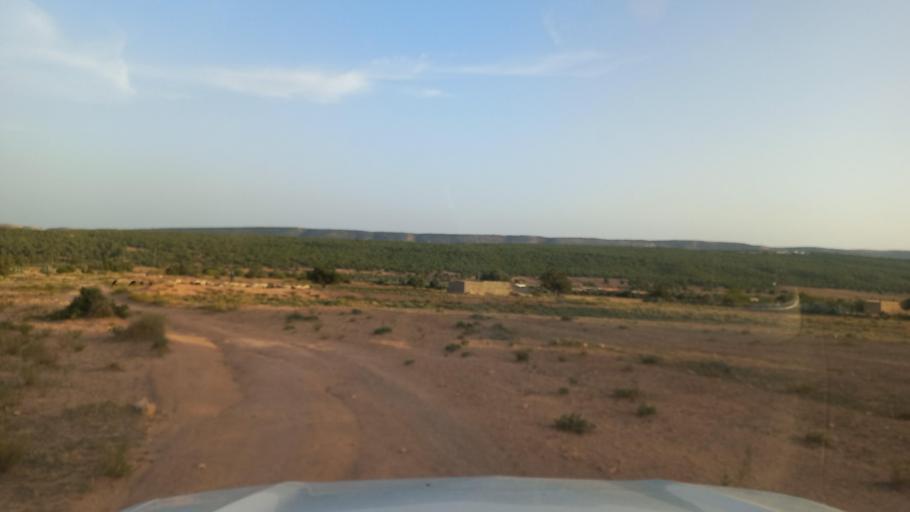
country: TN
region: Al Qasrayn
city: Sbiba
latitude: 35.4139
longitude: 8.9104
